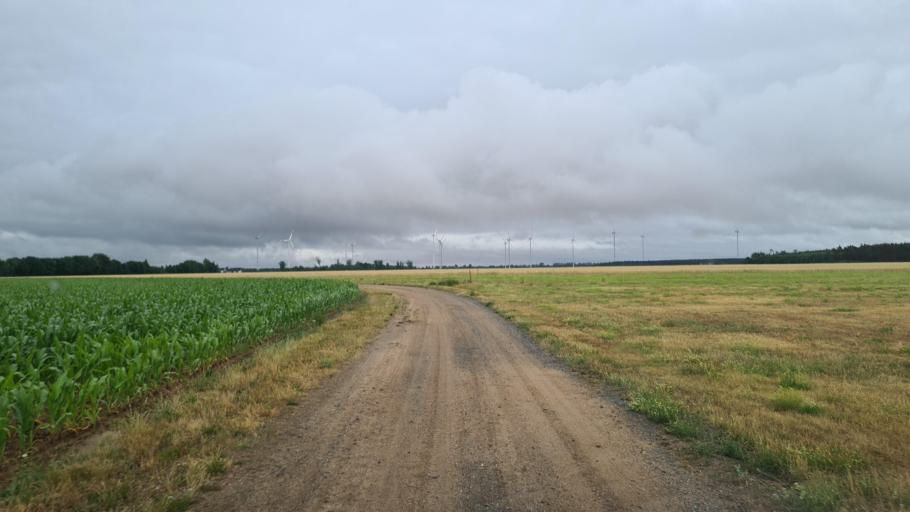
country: DE
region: Brandenburg
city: Bad Liebenwerda
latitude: 51.4969
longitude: 13.3221
